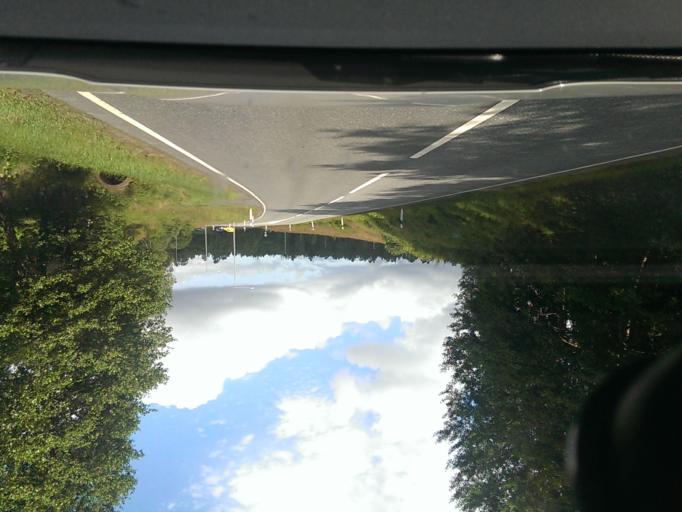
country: SE
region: Joenkoeping
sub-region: Varnamo Kommun
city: Varnamo
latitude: 57.2065
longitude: 14.0340
